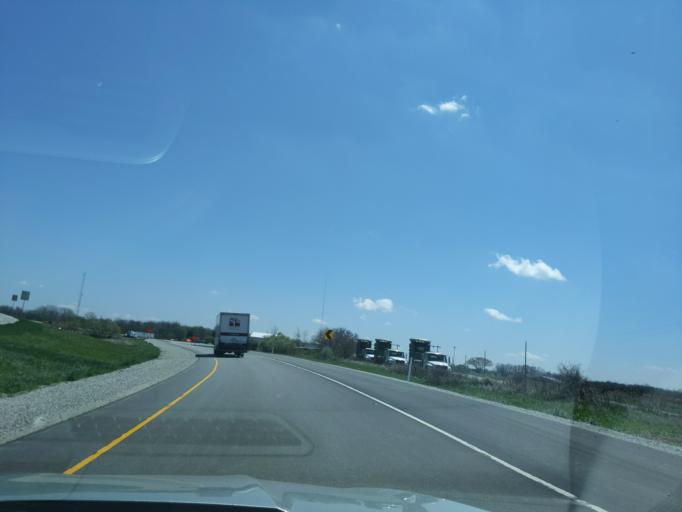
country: US
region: Indiana
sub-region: Boone County
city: Lebanon
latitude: 40.0731
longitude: -86.5020
